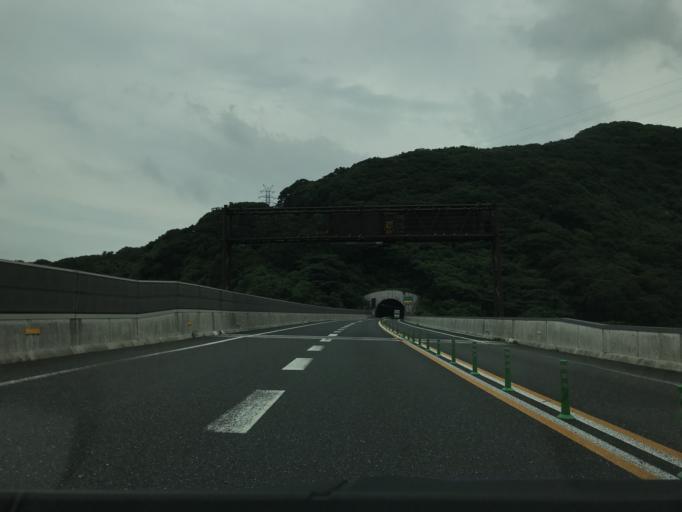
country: JP
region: Fukuoka
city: Kanda
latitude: 33.7926
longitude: 130.9685
